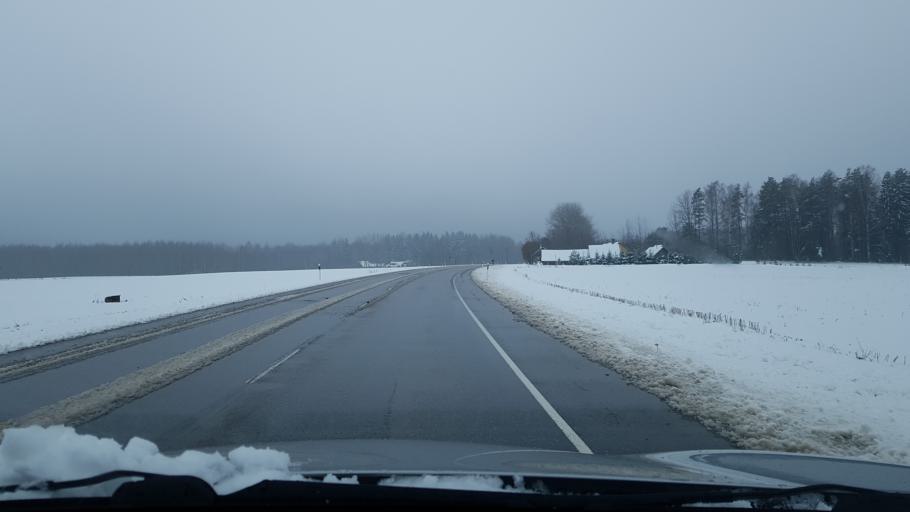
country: EE
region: Vorumaa
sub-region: Voru linn
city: Voru
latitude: 57.8584
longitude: 27.0898
